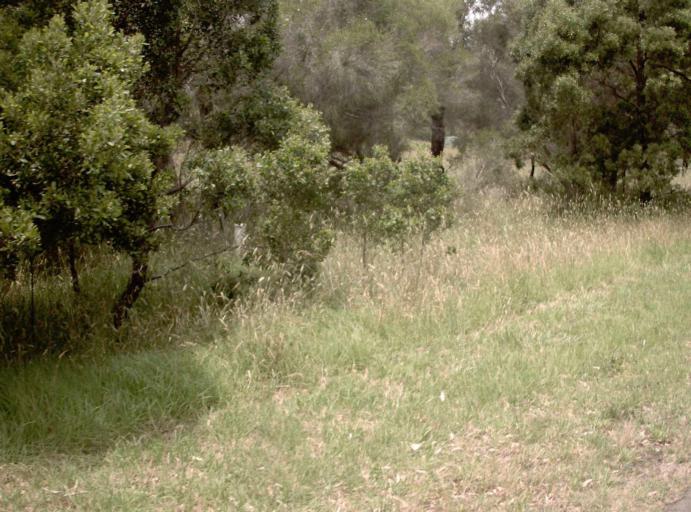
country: AU
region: Victoria
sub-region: Latrobe
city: Traralgon
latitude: -38.4692
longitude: 146.7178
